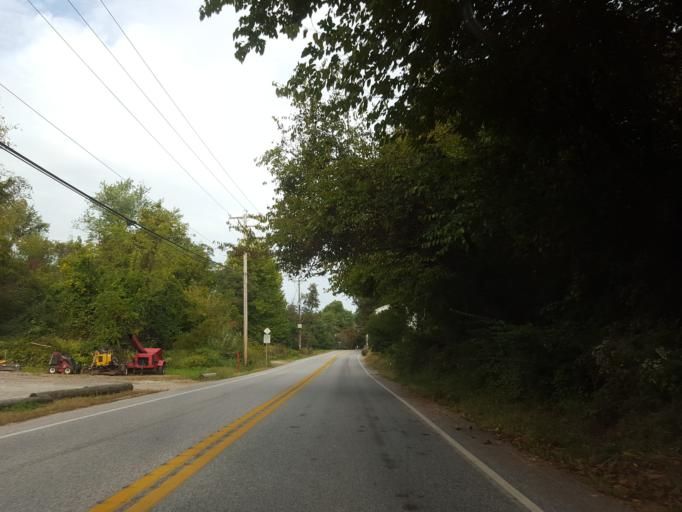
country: US
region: Pennsylvania
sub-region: York County
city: Yoe
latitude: 39.9132
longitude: -76.6401
